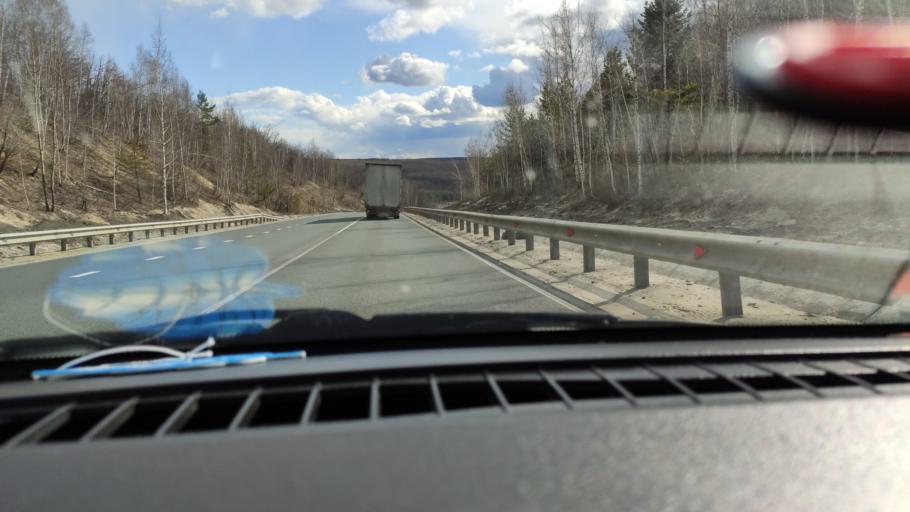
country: RU
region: Saratov
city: Alekseyevka
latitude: 52.4130
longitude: 48.0054
